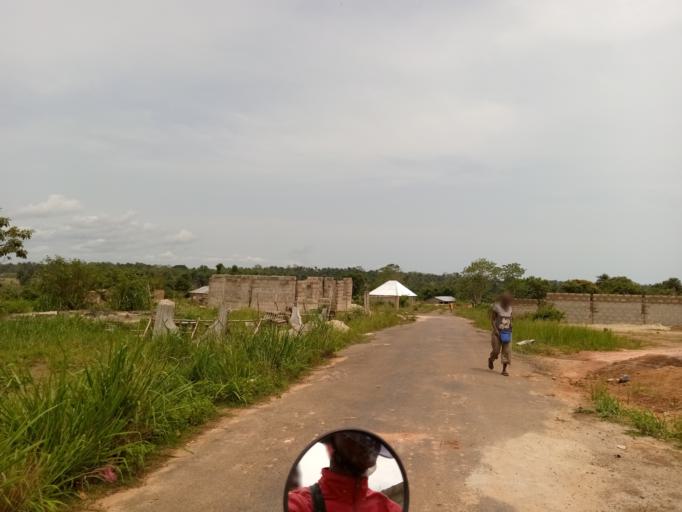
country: SL
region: Western Area
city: Waterloo
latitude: 8.3275
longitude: -13.0083
